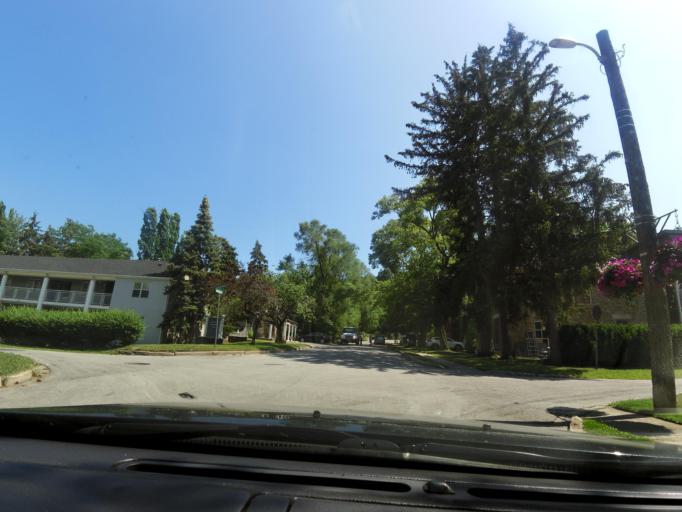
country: US
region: New York
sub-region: Niagara County
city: Lewiston
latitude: 43.1635
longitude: -79.0542
